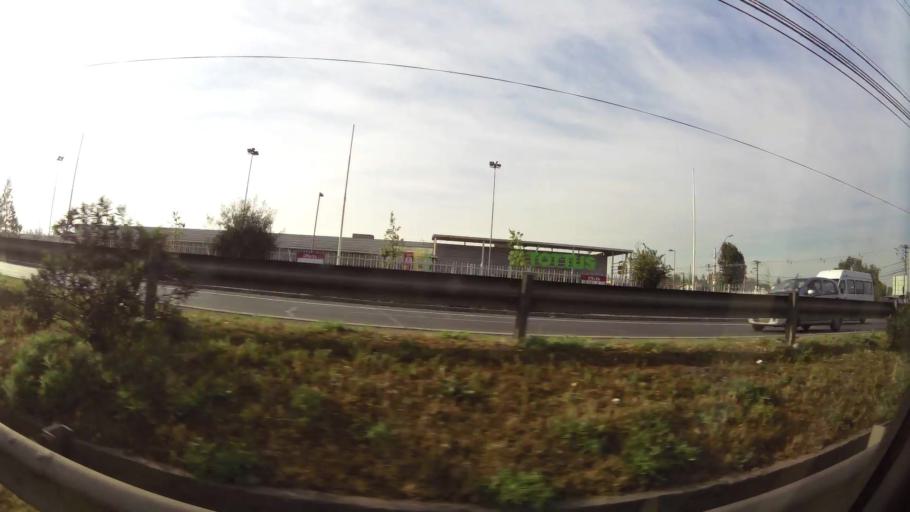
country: CL
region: Santiago Metropolitan
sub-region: Provincia de Talagante
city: Penaflor
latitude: -33.5714
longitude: -70.8184
